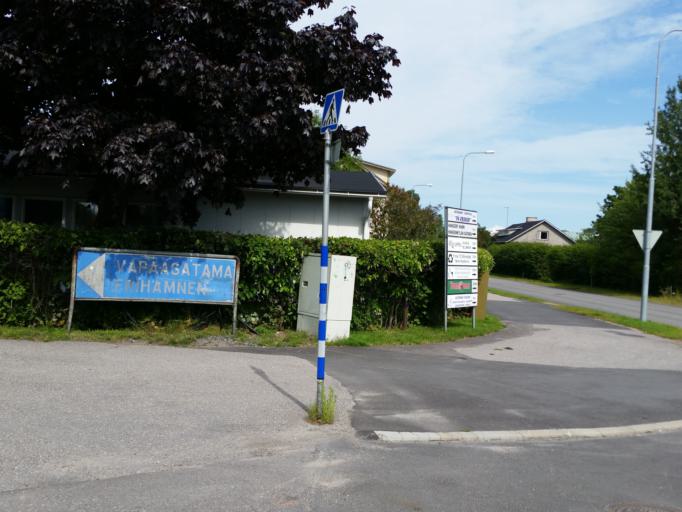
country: FI
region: Uusimaa
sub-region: Raaseporin
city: Hanko
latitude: 59.8289
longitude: 22.9474
